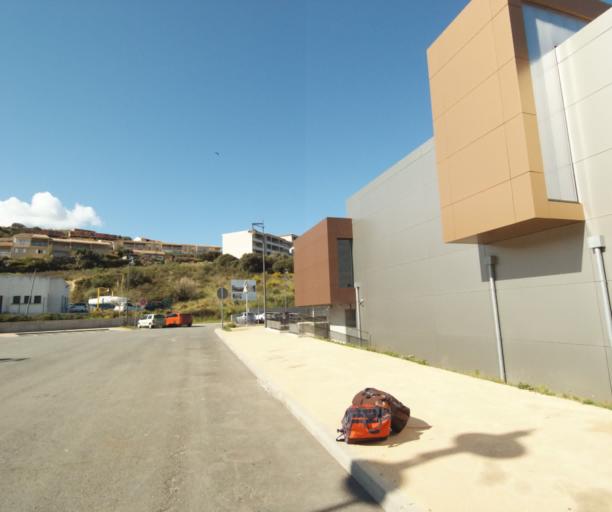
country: FR
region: Corsica
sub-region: Departement de la Corse-du-Sud
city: Propriano
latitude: 41.6731
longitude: 8.9007
